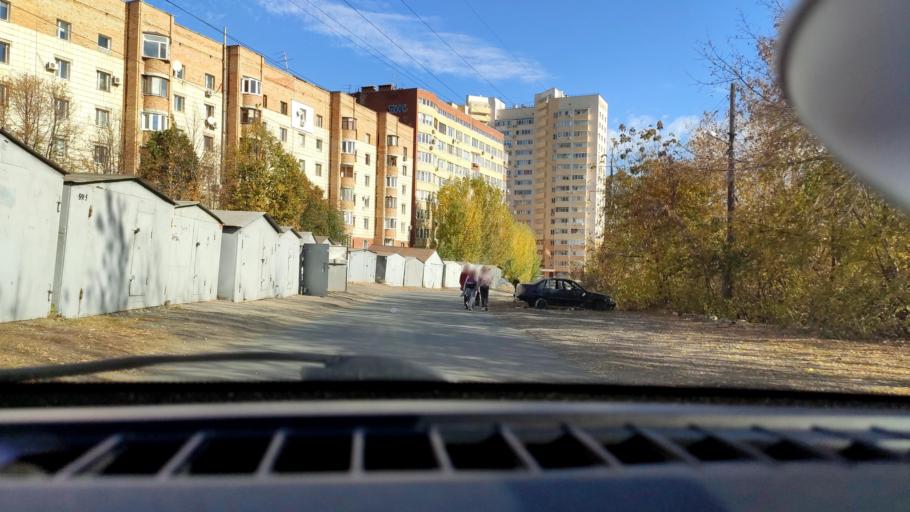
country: RU
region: Samara
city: Samara
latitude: 53.2109
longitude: 50.2096
